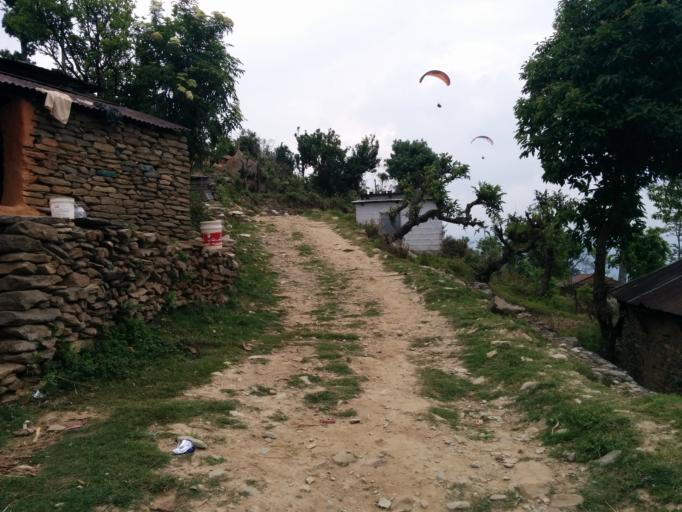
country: NP
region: Western Region
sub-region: Gandaki Zone
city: Pokhara
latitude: 28.2392
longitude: 83.9502
